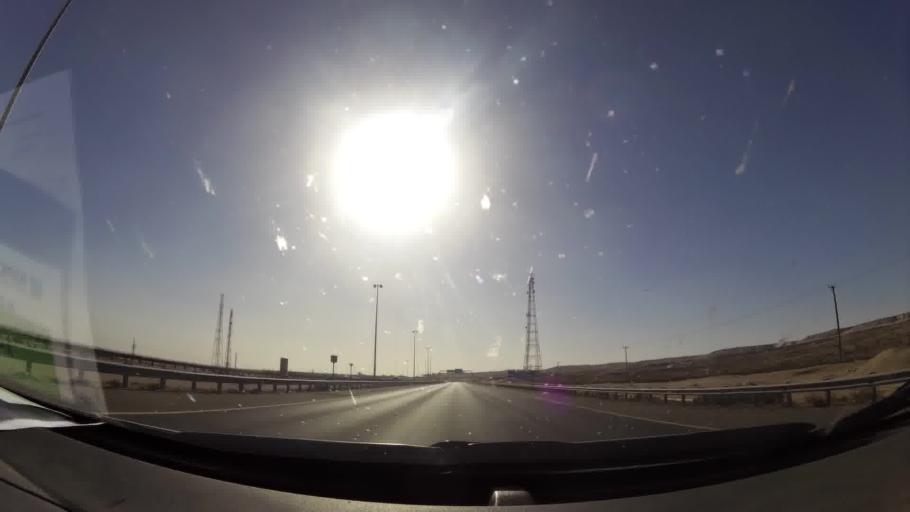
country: KW
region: Muhafazat al Jahra'
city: Al Jahra'
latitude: 29.4832
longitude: 47.7749
